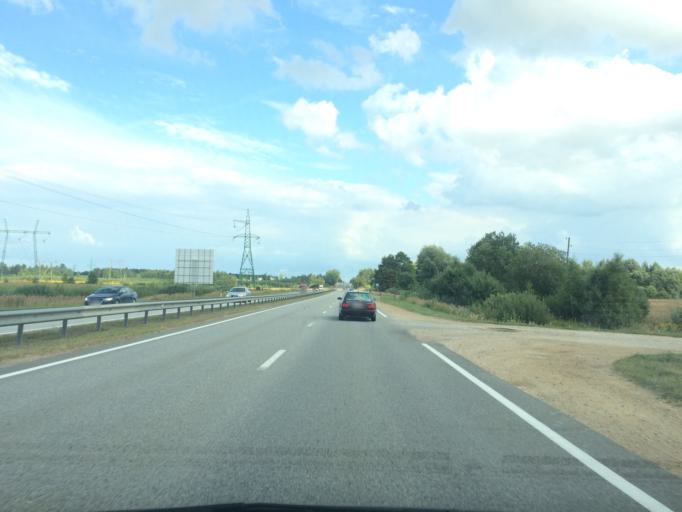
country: LV
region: Salaspils
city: Salaspils
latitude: 56.8465
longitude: 24.4054
